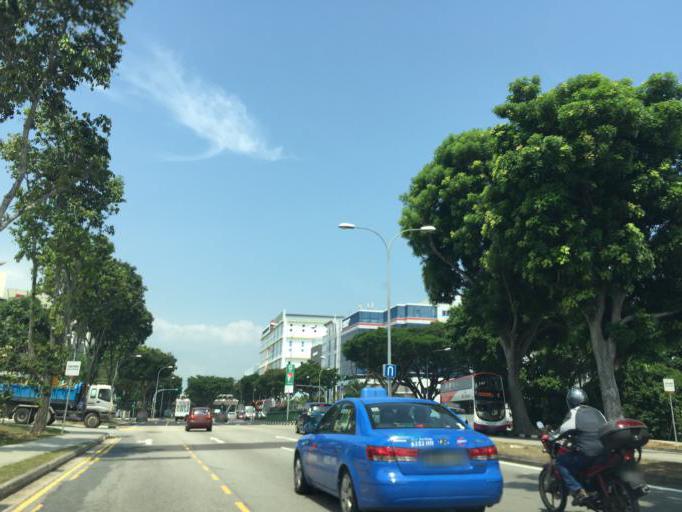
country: SG
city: Singapore
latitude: 1.3360
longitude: 103.9517
